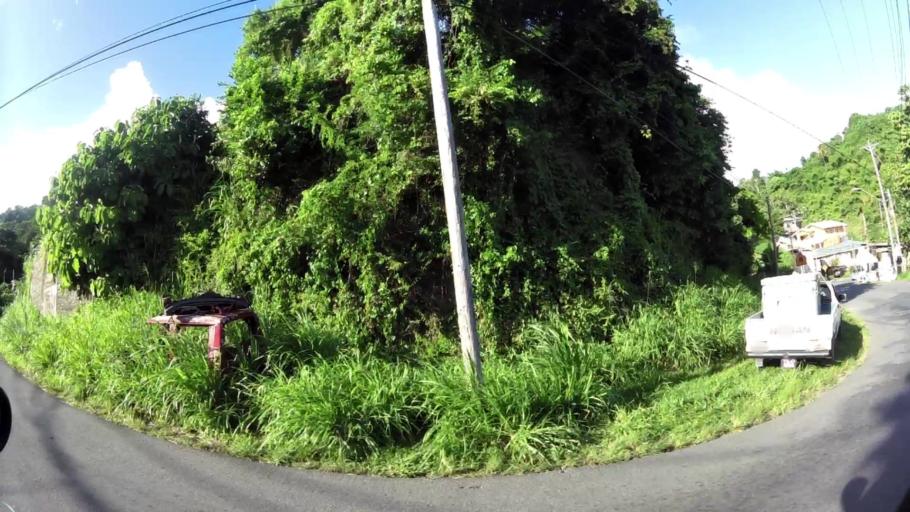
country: TT
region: Eastern Tobago
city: Roxborough
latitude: 11.2317
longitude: -60.6034
